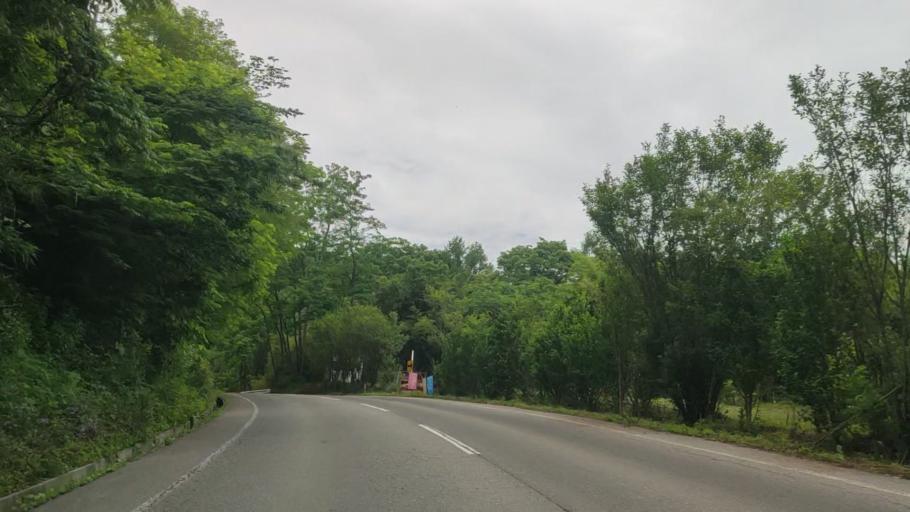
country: JP
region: Nagano
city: Kamimaruko
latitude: 36.3158
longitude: 138.3324
